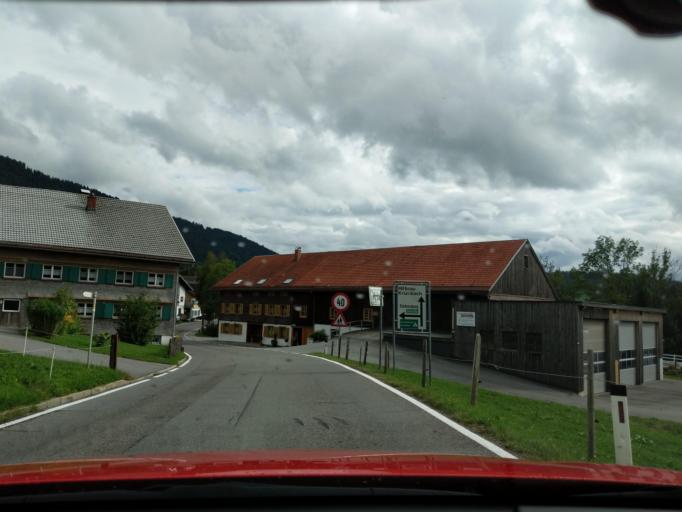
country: AT
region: Vorarlberg
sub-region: Politischer Bezirk Bregenz
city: Krumbach
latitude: 47.5010
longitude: 9.9460
